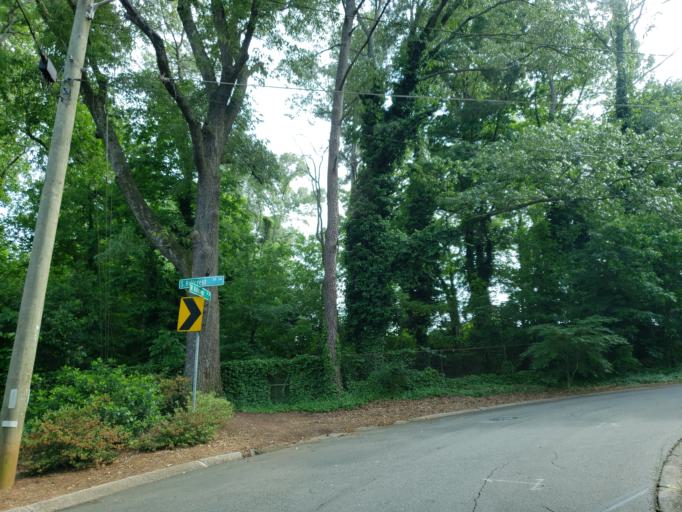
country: US
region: Georgia
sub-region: Cobb County
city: Marietta
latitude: 33.9454
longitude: -84.5571
